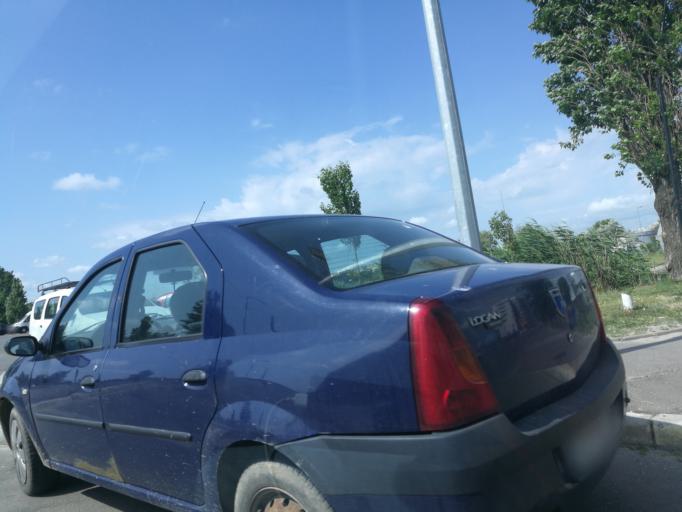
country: RO
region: Constanta
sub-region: Municipiul Constanta
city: Constanta
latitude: 44.2164
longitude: 28.6409
